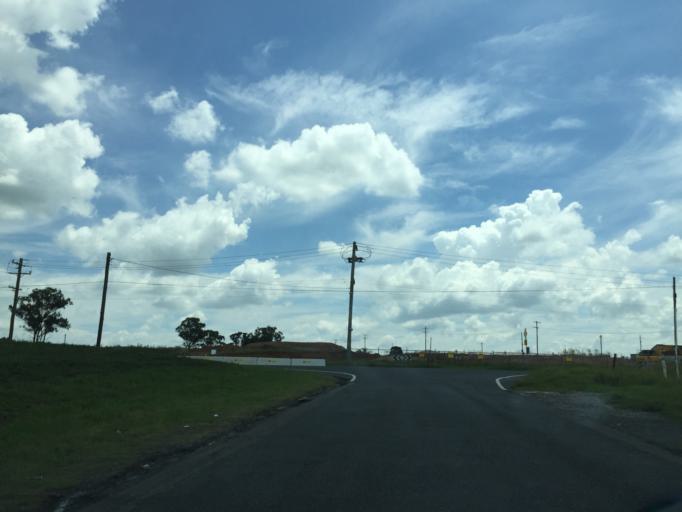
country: AU
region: New South Wales
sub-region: Blacktown
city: Riverstone
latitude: -33.6978
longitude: 150.8874
